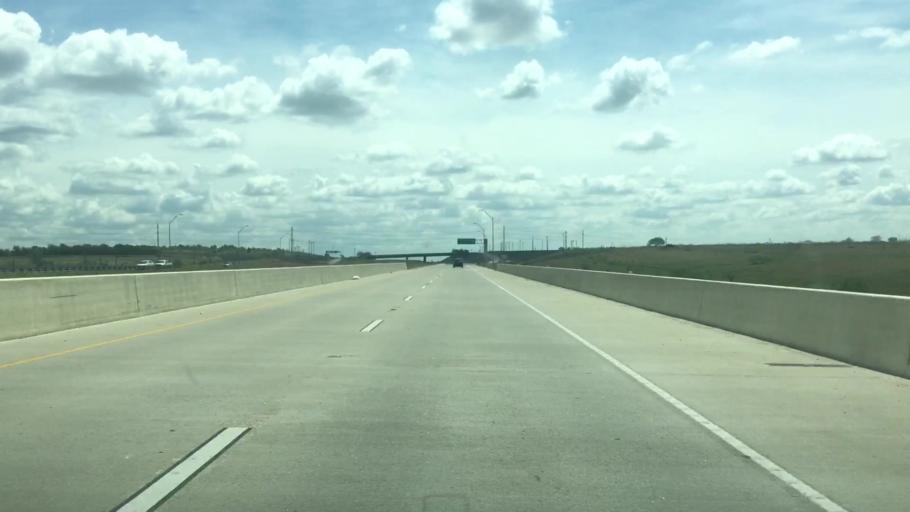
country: US
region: Texas
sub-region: Travis County
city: Onion Creek
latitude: 30.1068
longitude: -97.7899
